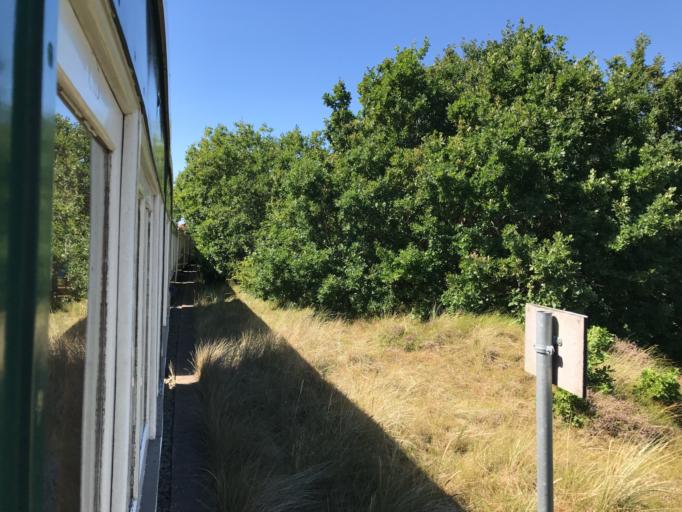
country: DE
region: Lower Saxony
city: Borkum
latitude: 53.5794
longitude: 6.6764
